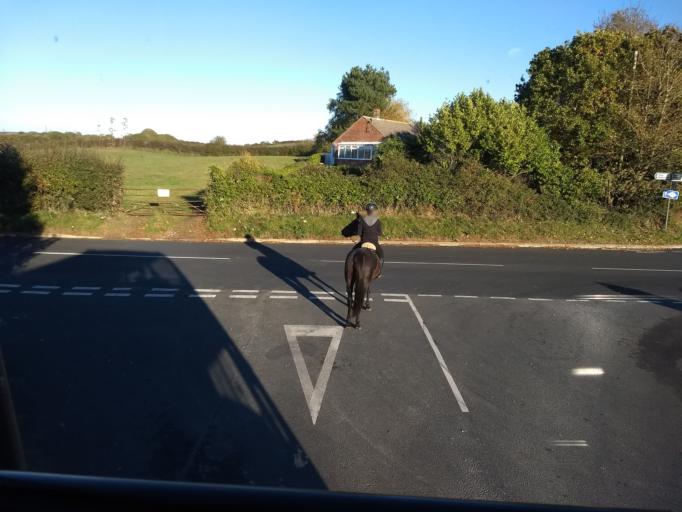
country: GB
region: England
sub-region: Isle of Wight
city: Newchurch
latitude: 50.6548
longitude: -1.2112
